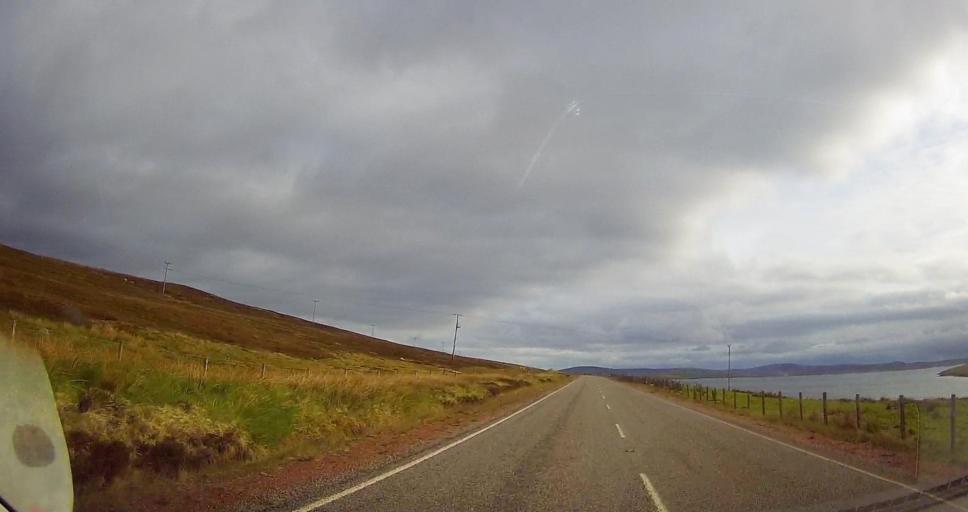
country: GB
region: Scotland
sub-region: Shetland Islands
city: Lerwick
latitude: 60.4558
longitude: -1.2118
